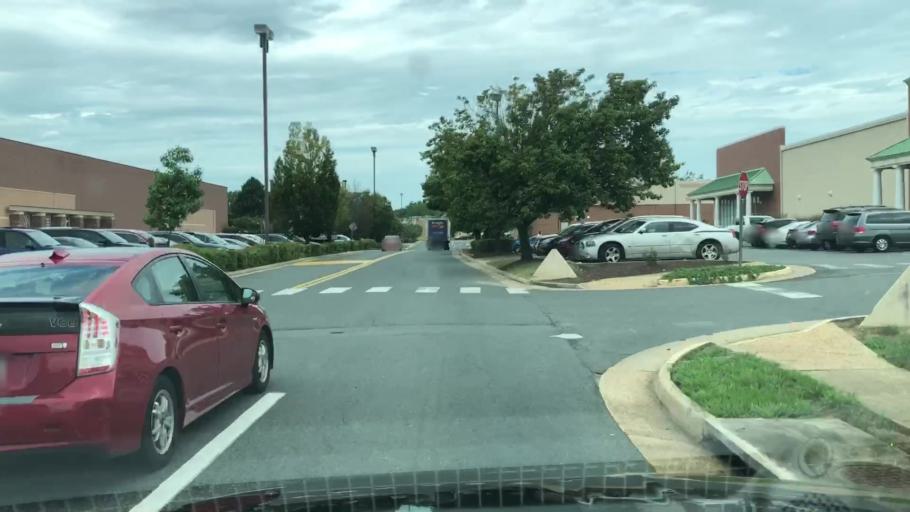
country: US
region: Virginia
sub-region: Stafford County
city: Falmouth
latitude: 38.3000
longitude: -77.5119
